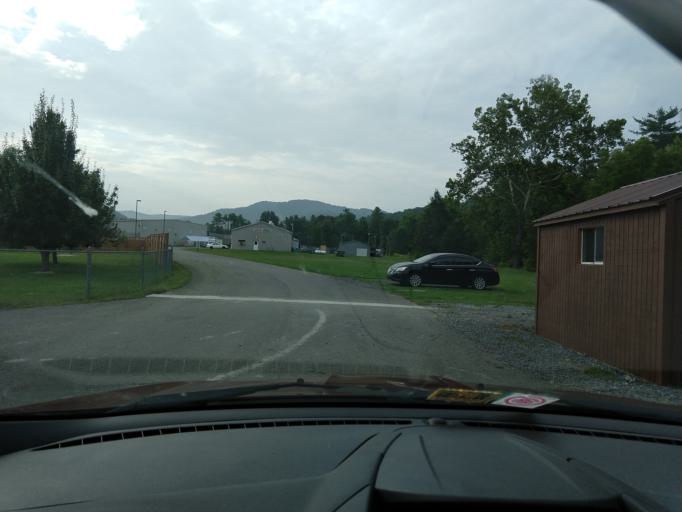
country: US
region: Virginia
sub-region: City of Covington
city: Covington
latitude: 37.9650
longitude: -80.1292
